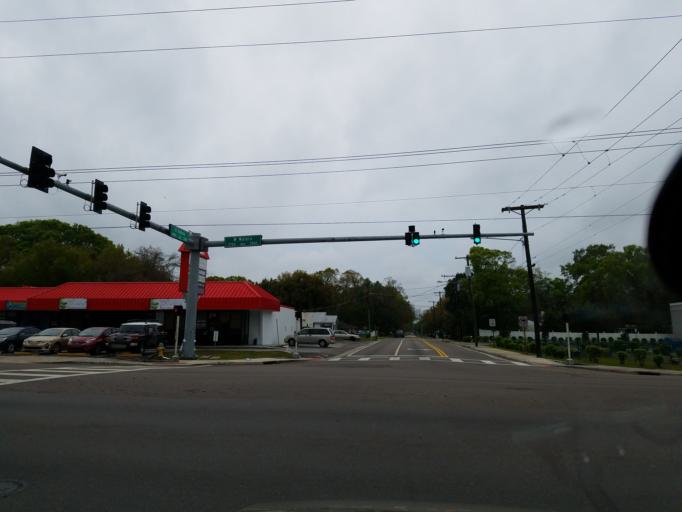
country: US
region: Florida
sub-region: Hillsborough County
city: Egypt Lake-Leto
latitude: 28.0254
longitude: -82.4884
